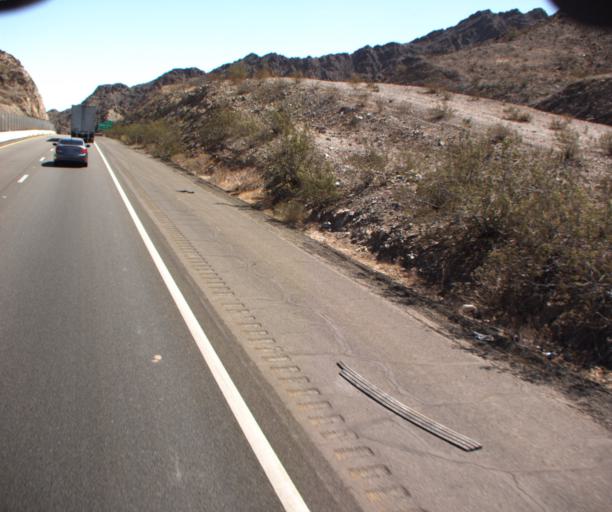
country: US
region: Arizona
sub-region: Yuma County
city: Fortuna Foothills
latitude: 32.6605
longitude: -114.3275
